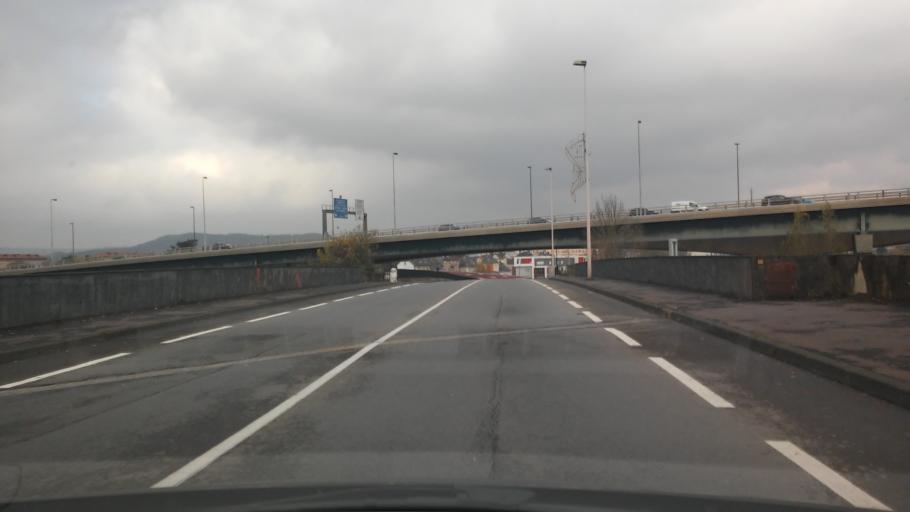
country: FR
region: Lorraine
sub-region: Departement de la Moselle
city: Thionville
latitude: 49.3472
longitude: 6.1606
